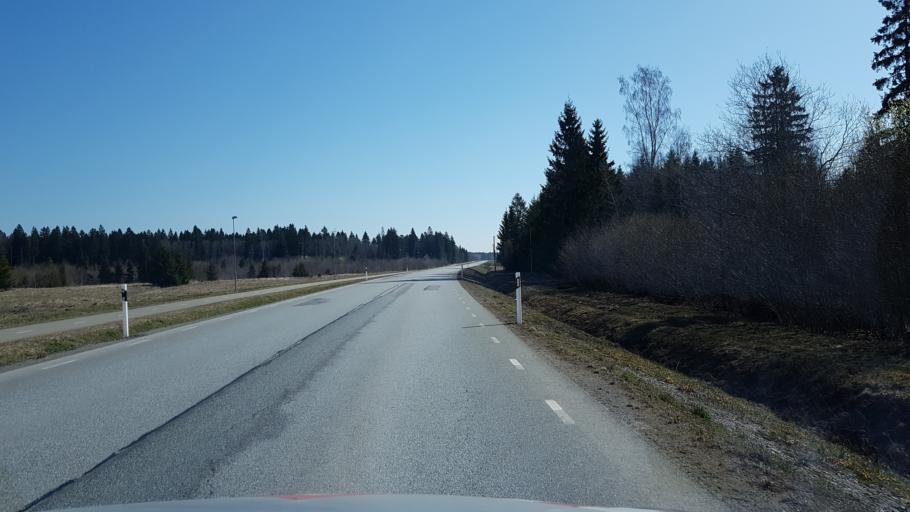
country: EE
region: Ida-Virumaa
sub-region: Kivioli linn
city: Kivioli
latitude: 59.3542
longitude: 26.8761
